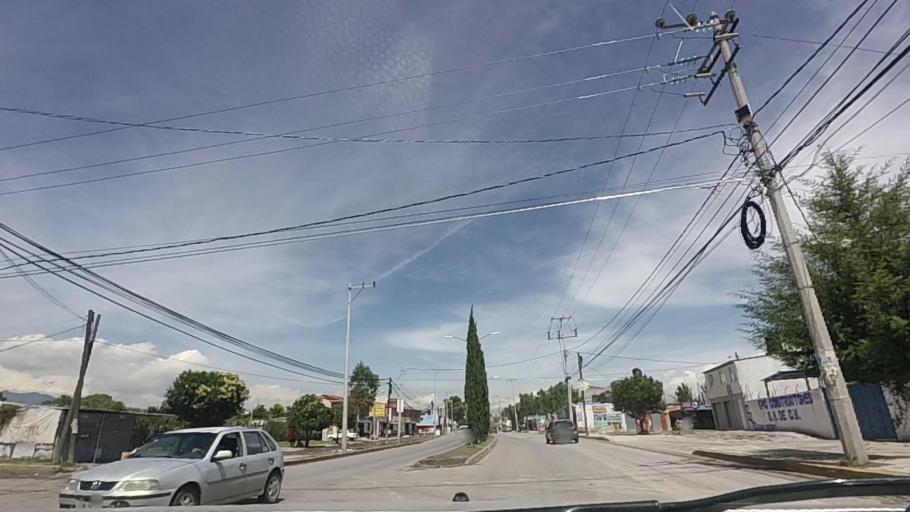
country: MX
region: Mexico
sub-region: Huehuetoca
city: Casa Nueva
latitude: 19.8314
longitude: -99.2153
